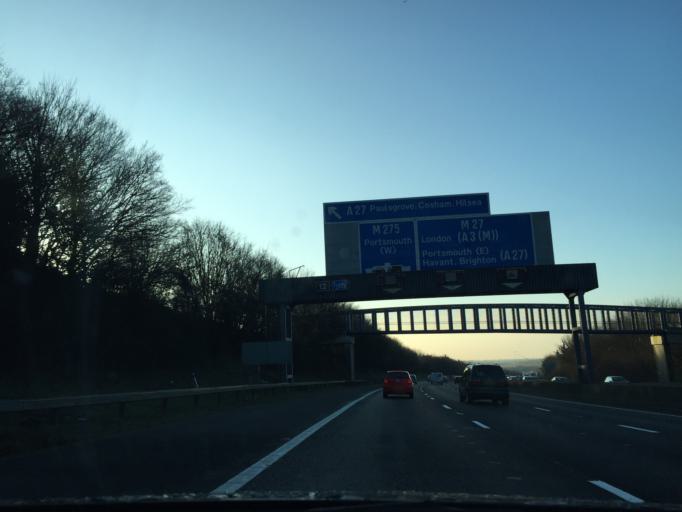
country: GB
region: England
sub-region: Portsmouth
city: Cosham
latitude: 50.8530
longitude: -1.1074
